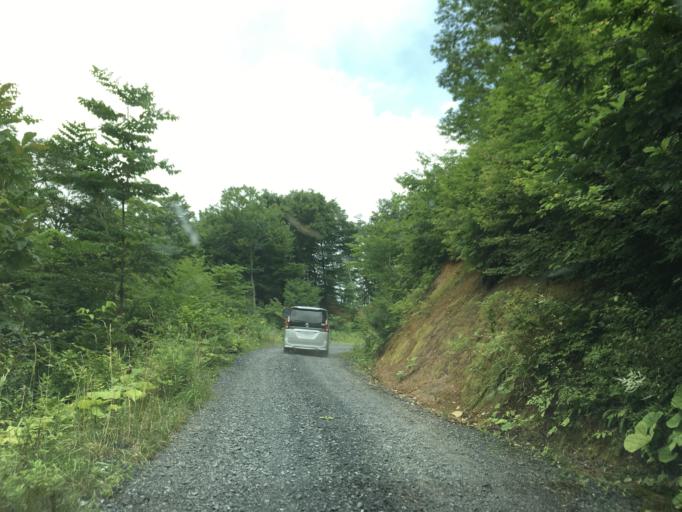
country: JP
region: Iwate
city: Ichinoseki
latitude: 38.9455
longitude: 140.8675
